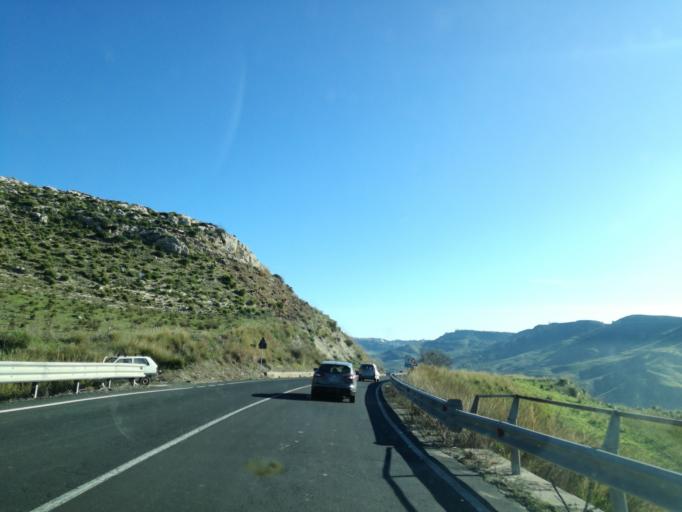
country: IT
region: Sicily
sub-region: Catania
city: San Michele di Ganzaria
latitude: 37.2272
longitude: 14.4345
